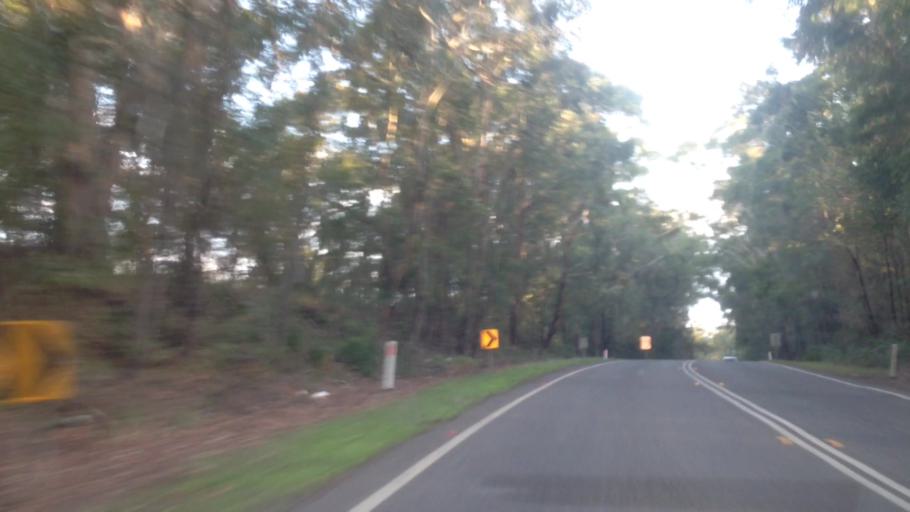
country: AU
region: New South Wales
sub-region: Lake Macquarie Shire
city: Cooranbong
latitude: -32.9789
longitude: 151.4838
